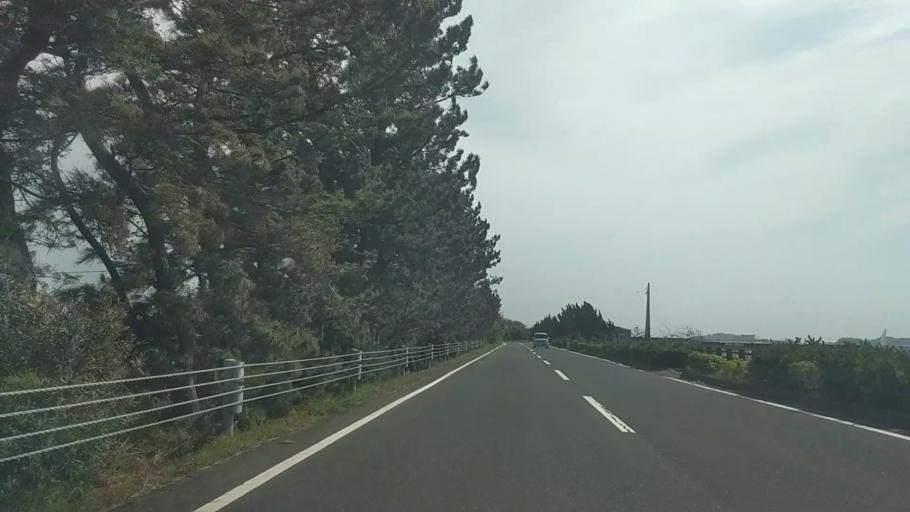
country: JP
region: Shizuoka
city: Kosai-shi
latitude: 34.7156
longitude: 137.5847
